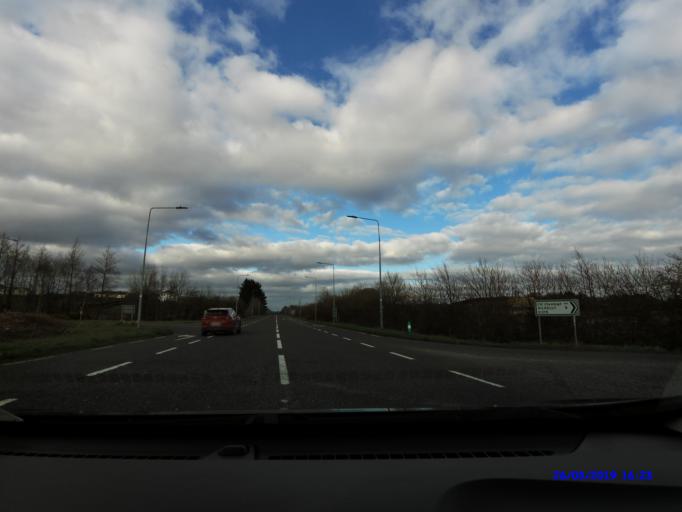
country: IE
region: Connaught
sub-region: Maigh Eo
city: Swinford
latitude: 53.9359
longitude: -8.9406
